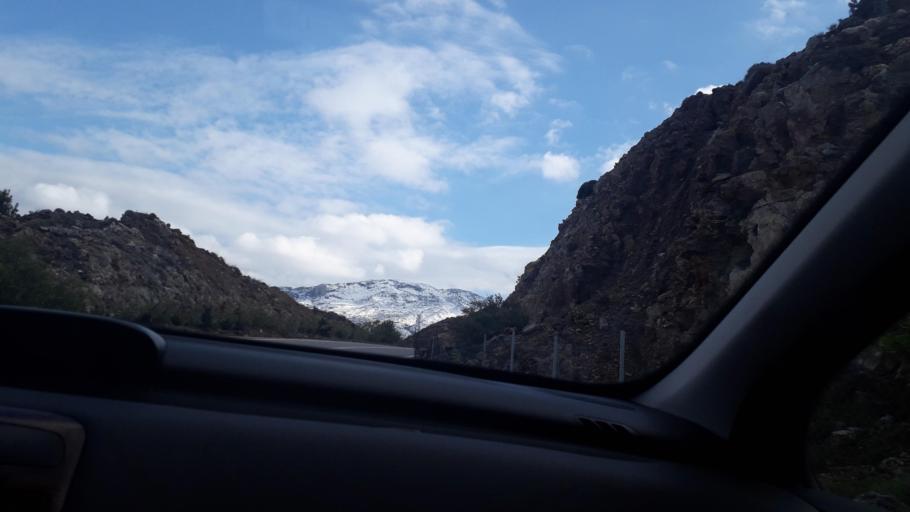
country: GR
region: Crete
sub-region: Nomos Rethymnis
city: Agia Foteini
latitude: 35.2659
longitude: 24.5640
